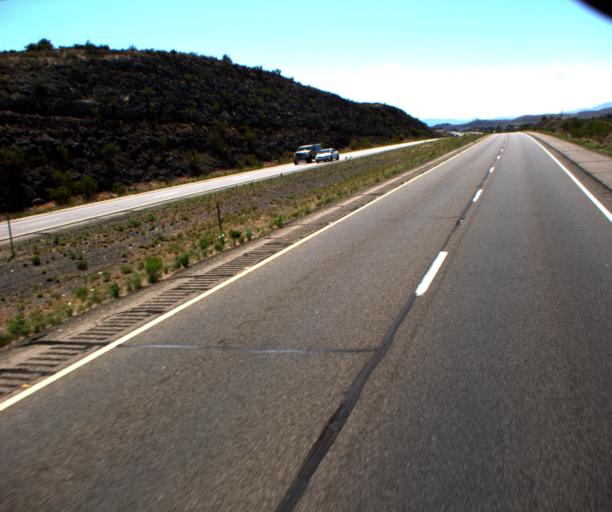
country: US
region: Arizona
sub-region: Yavapai County
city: Spring Valley
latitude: 34.3666
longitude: -112.1785
